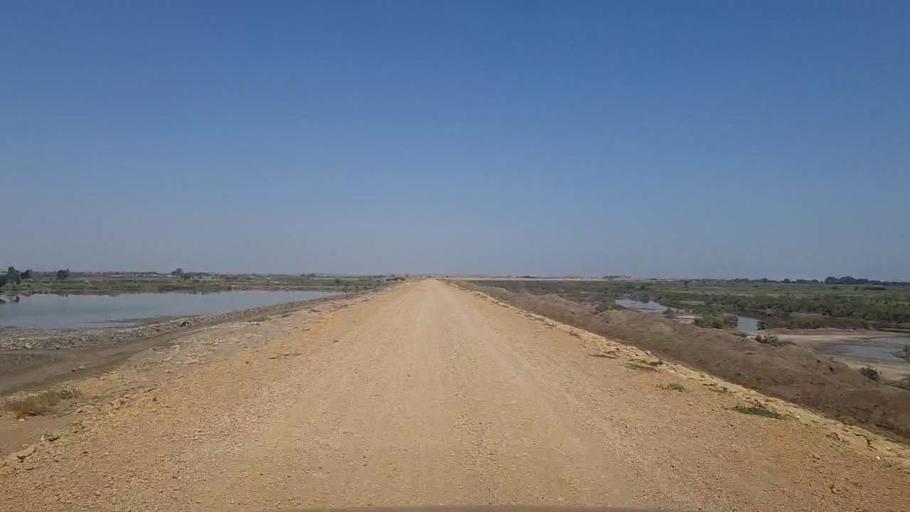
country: PK
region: Sindh
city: Thatta
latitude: 24.7919
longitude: 67.9978
